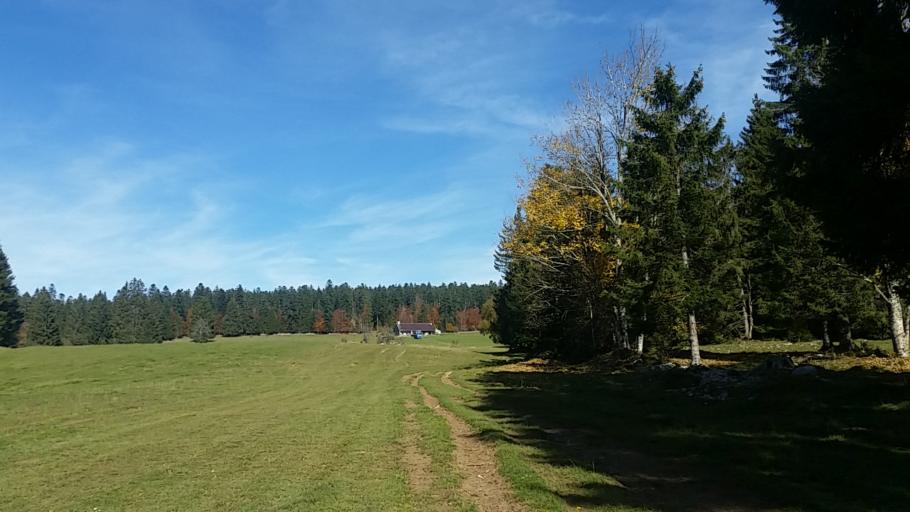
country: FR
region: Franche-Comte
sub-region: Departement du Doubs
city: Jougne
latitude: 46.7731
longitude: 6.4076
